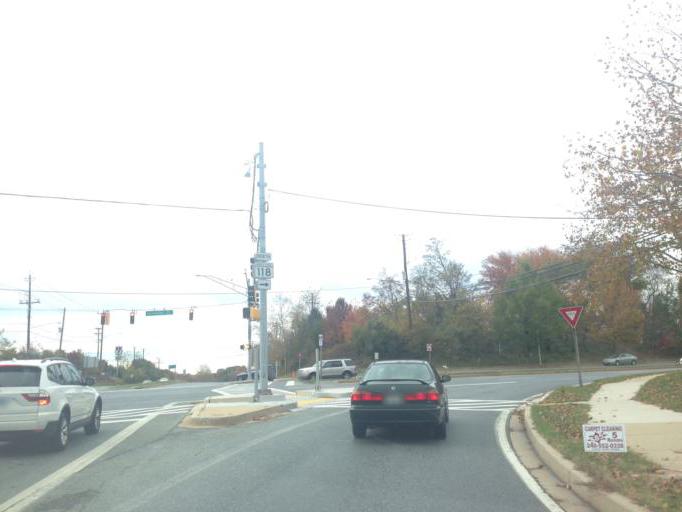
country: US
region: Maryland
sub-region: Montgomery County
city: Germantown
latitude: 39.1627
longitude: -77.2825
